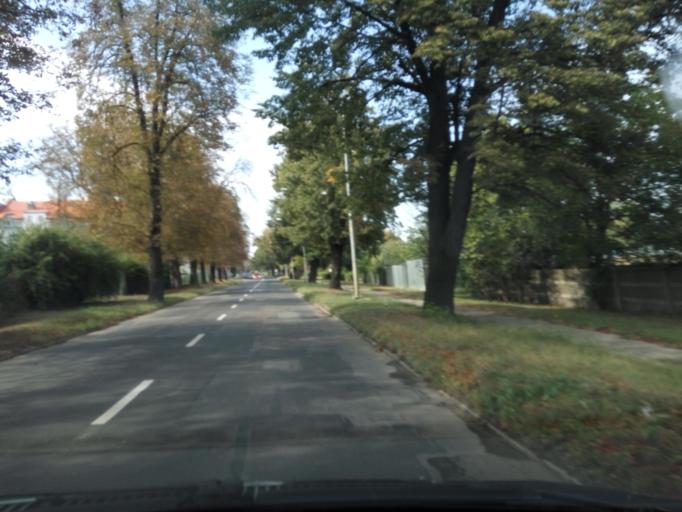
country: PL
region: Lower Silesian Voivodeship
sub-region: Powiat wroclawski
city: Radwanice
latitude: 51.0608
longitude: 17.0858
